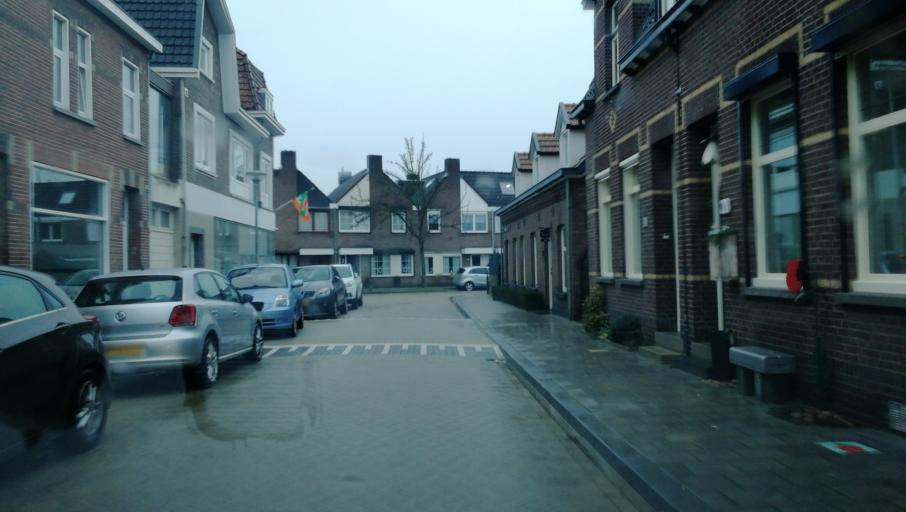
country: NL
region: Limburg
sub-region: Gemeente Venlo
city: Venlo
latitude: 51.3693
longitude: 6.1517
